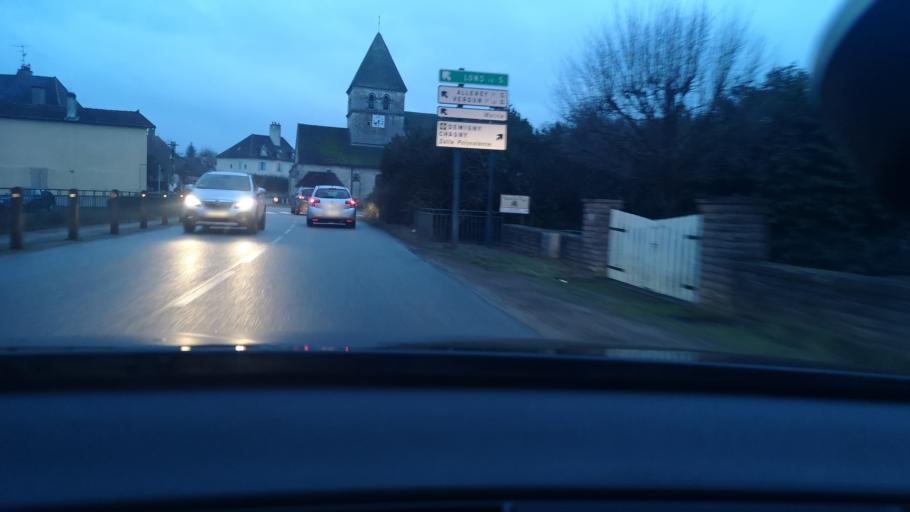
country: FR
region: Bourgogne
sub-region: Departement de Saone-et-Loire
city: Demigny
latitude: 46.9484
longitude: 4.9086
